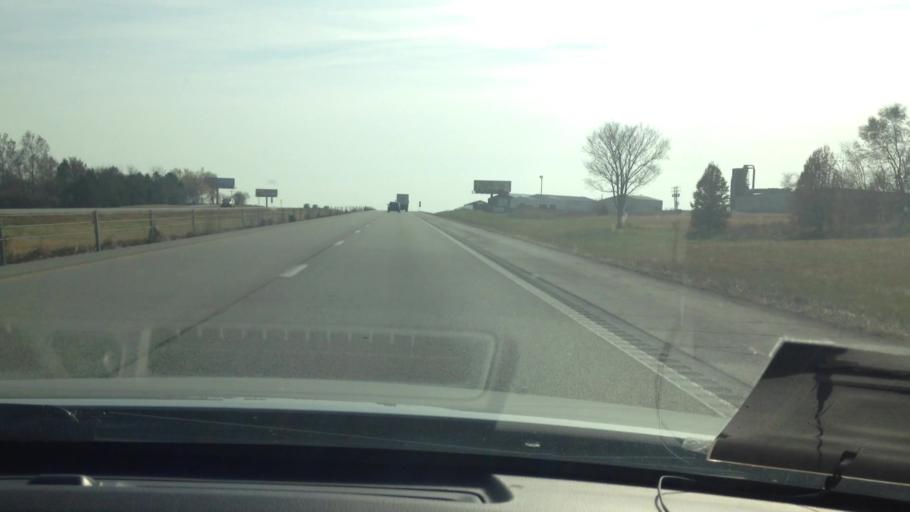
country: US
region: Missouri
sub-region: Cass County
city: Peculiar
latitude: 38.7125
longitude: -94.4453
